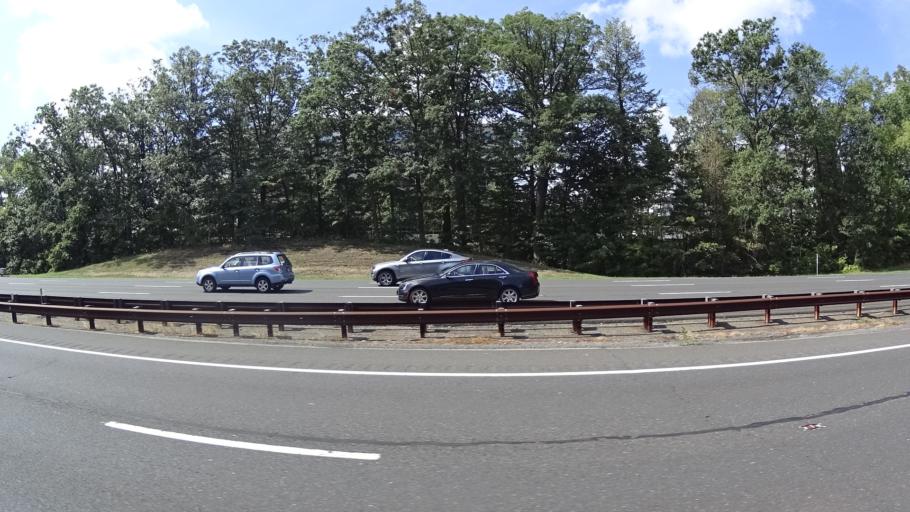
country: US
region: New Jersey
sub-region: Middlesex County
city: Laurence Harbor
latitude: 40.4326
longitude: -74.2487
